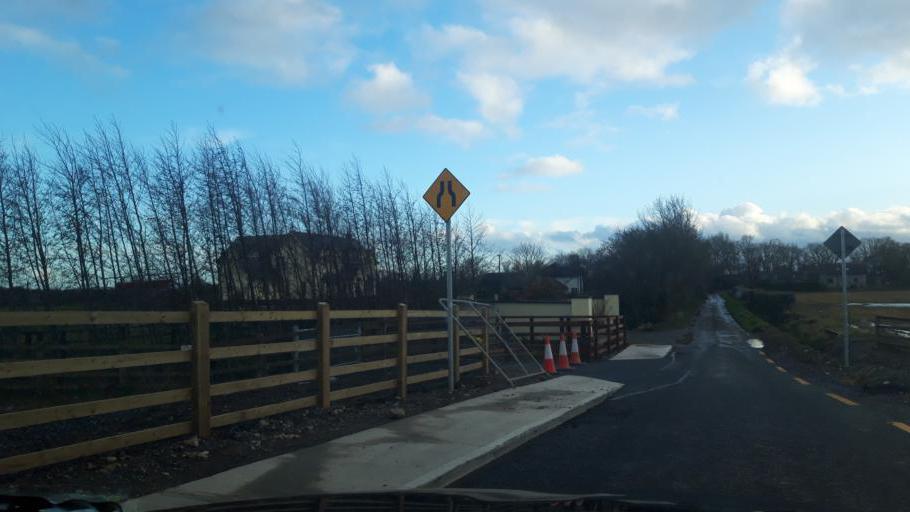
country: IE
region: Leinster
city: Donabate
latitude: 53.4788
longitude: -6.1628
